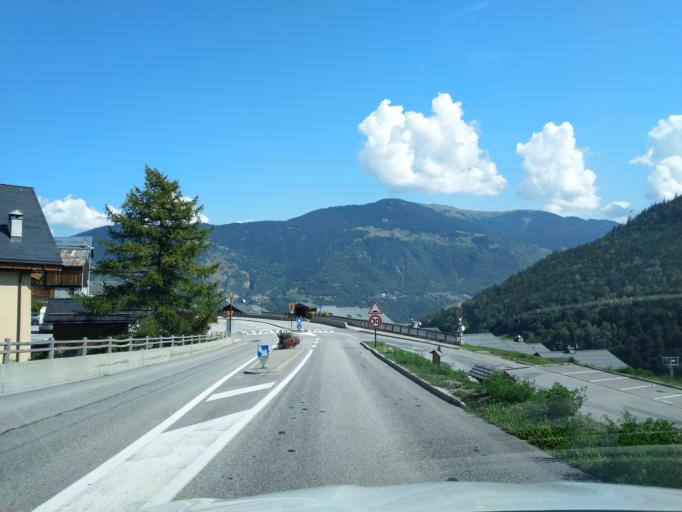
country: FR
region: Rhone-Alpes
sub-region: Departement de la Savoie
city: Les Allues
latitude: 45.4312
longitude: 6.5573
